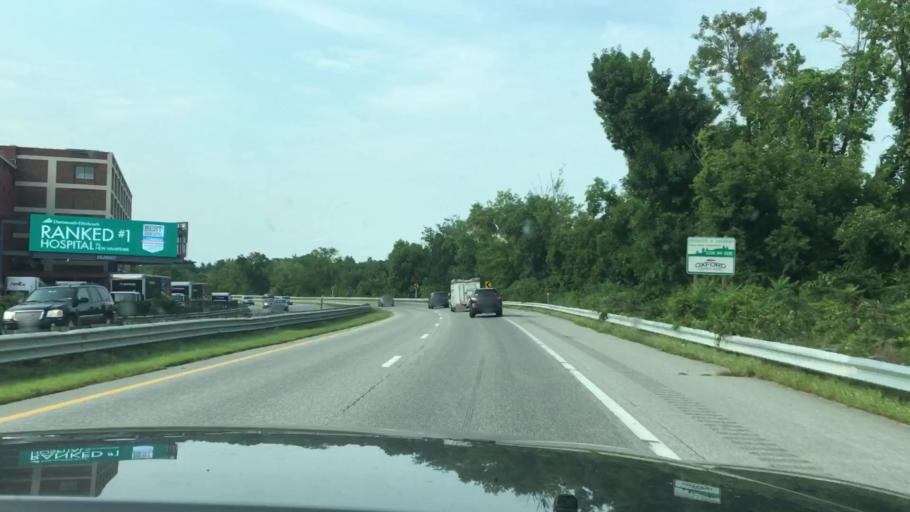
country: US
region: New Hampshire
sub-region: Hillsborough County
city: Manchester
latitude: 42.9949
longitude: -71.4706
